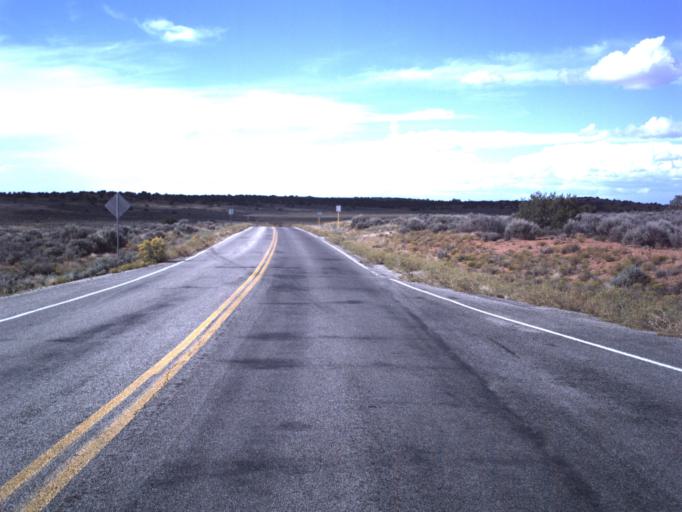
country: US
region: Utah
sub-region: Grand County
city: Moab
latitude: 38.5168
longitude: -109.7301
